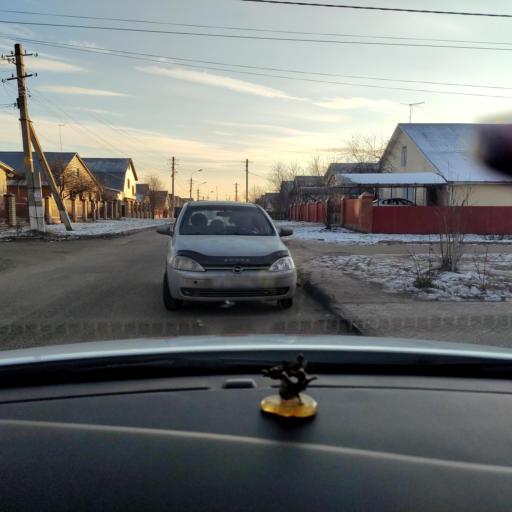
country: RU
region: Tatarstan
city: Stolbishchi
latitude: 55.6113
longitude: 49.1366
